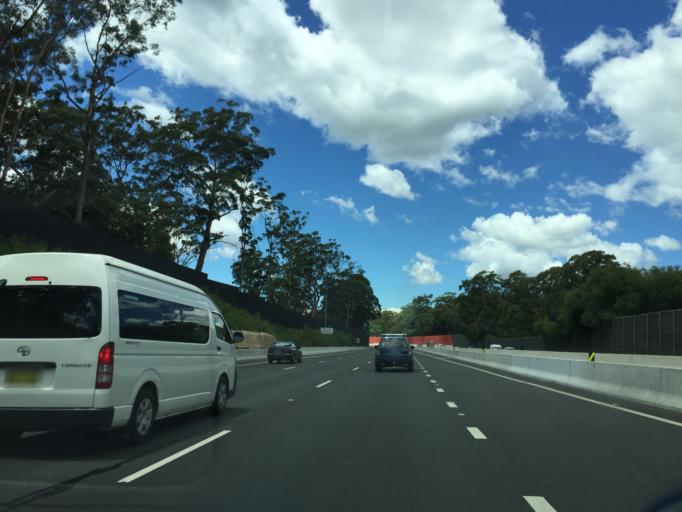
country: AU
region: New South Wales
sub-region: Hornsby Shire
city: Beecroft
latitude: -33.7591
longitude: 151.0664
